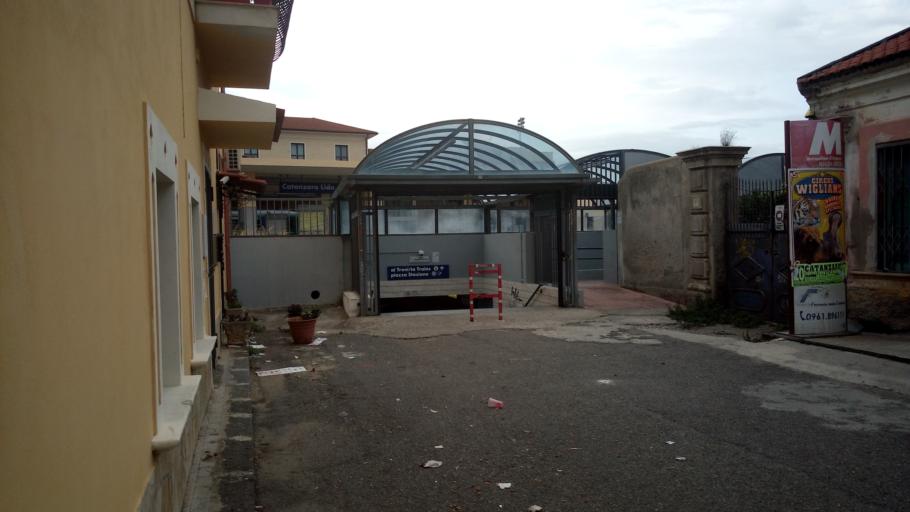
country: IT
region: Calabria
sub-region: Provincia di Catanzaro
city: Roccelletta
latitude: 38.8214
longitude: 16.6132
